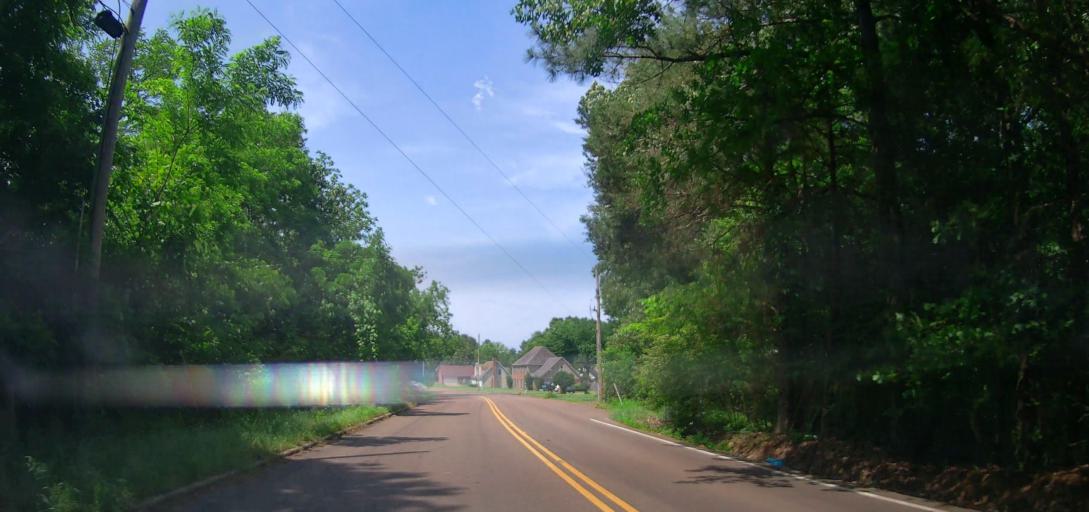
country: US
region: Mississippi
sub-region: De Soto County
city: Olive Branch
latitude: 35.0098
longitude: -89.8294
